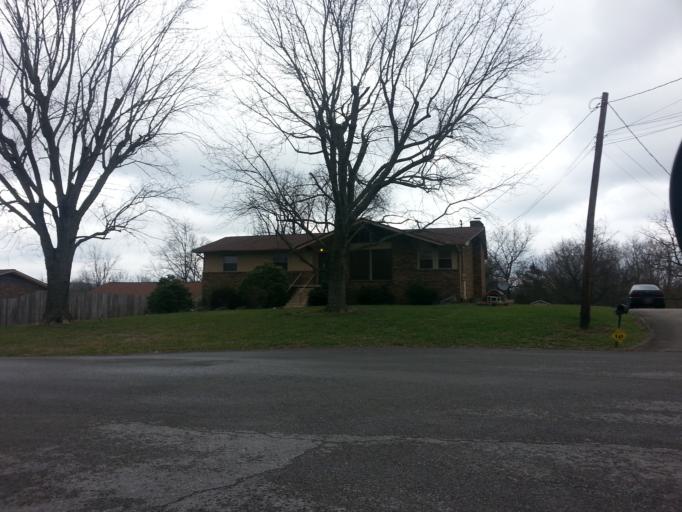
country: US
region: Tennessee
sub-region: Knox County
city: Knoxville
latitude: 36.0790
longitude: -83.9360
